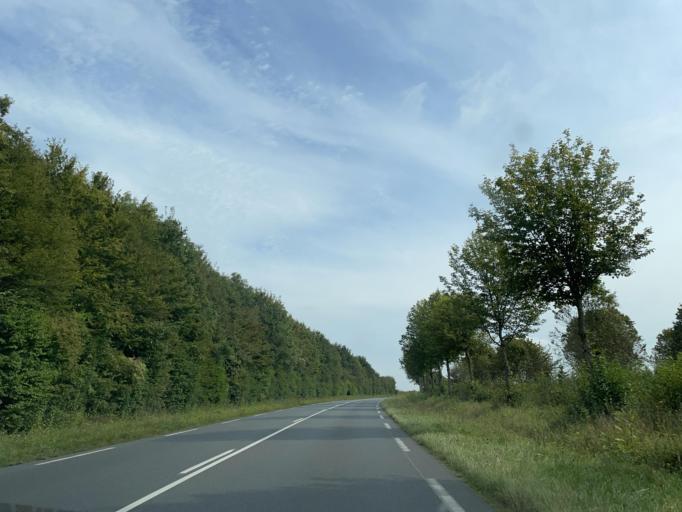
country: FR
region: Ile-de-France
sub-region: Departement de Seine-et-Marne
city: Nanteuil-les-Meaux
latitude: 48.9132
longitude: 2.9040
